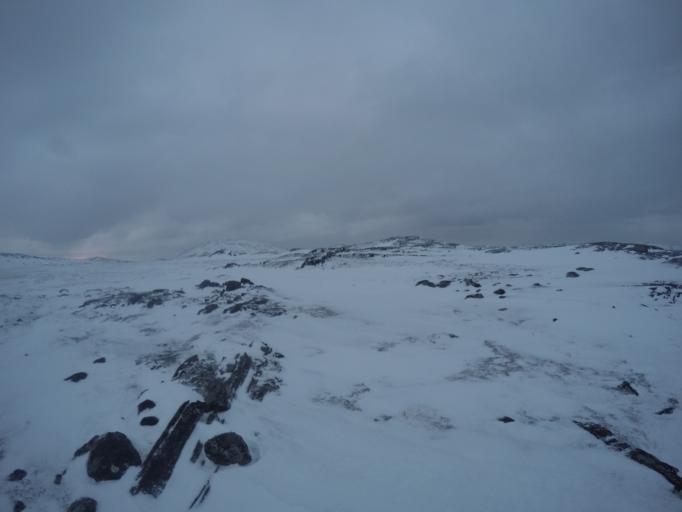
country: GL
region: Sermersooq
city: Nuuk
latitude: 64.1385
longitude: -51.6739
